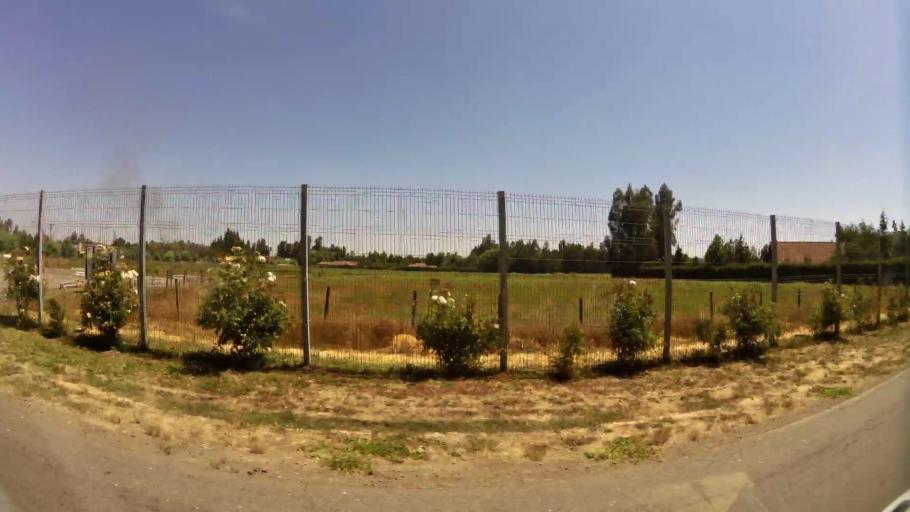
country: CL
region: Maule
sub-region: Provincia de Curico
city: Curico
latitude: -35.0004
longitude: -71.2097
